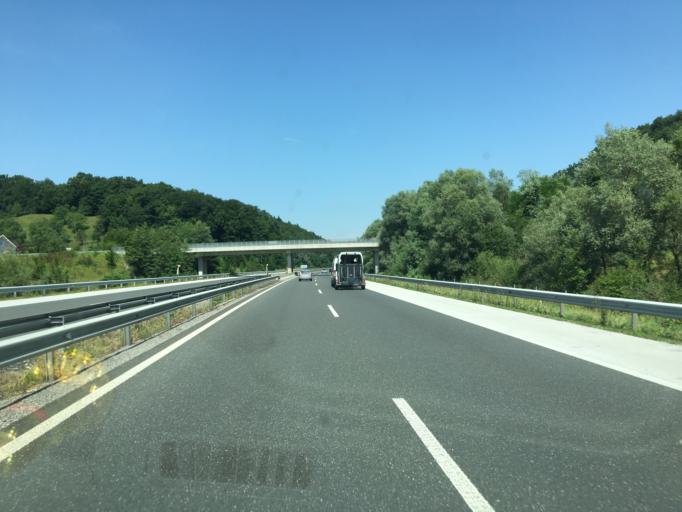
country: SI
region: Pesnica
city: Pesnica pri Mariboru
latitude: 46.6203
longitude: 15.6590
